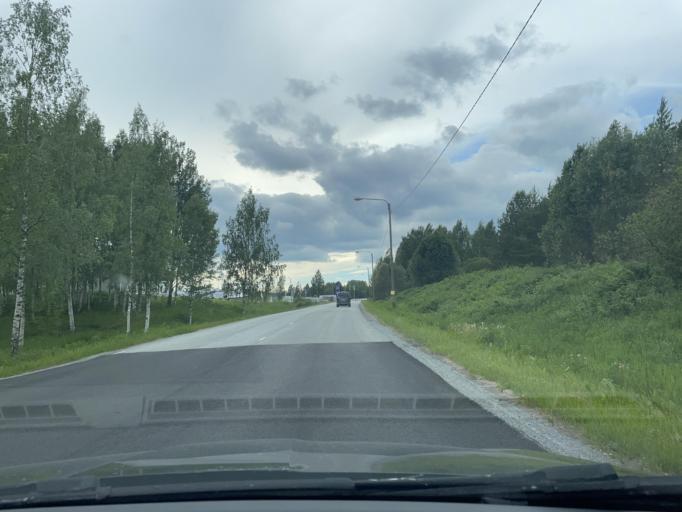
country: FI
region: Central Finland
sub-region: Jaemsae
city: Jaemsae
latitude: 61.8573
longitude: 25.1878
